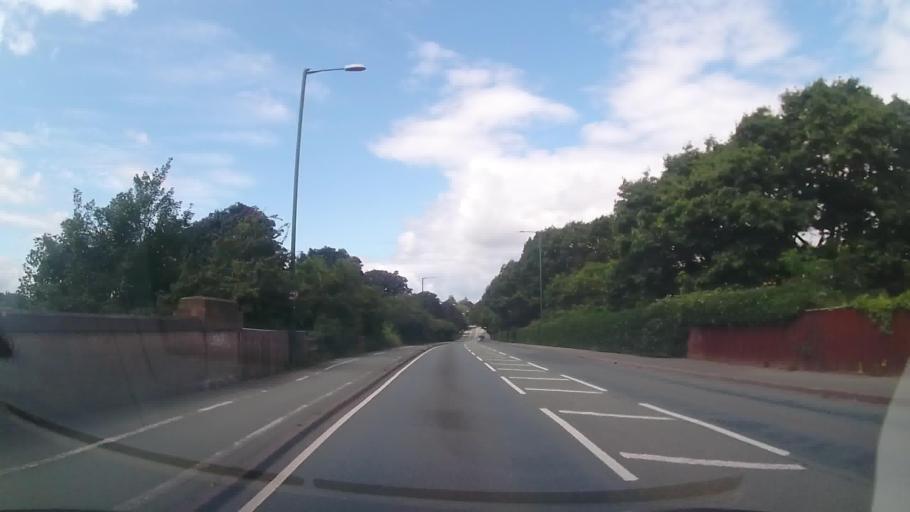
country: GB
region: England
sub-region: Shropshire
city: Shrewsbury
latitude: 52.6941
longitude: -2.7596
